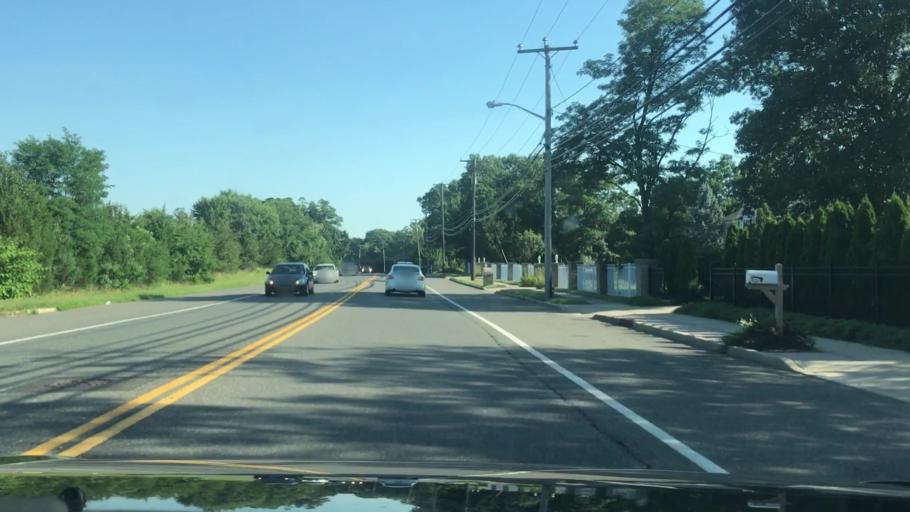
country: US
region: New Jersey
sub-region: Ocean County
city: Leisure Village
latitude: 40.0095
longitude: -74.2025
